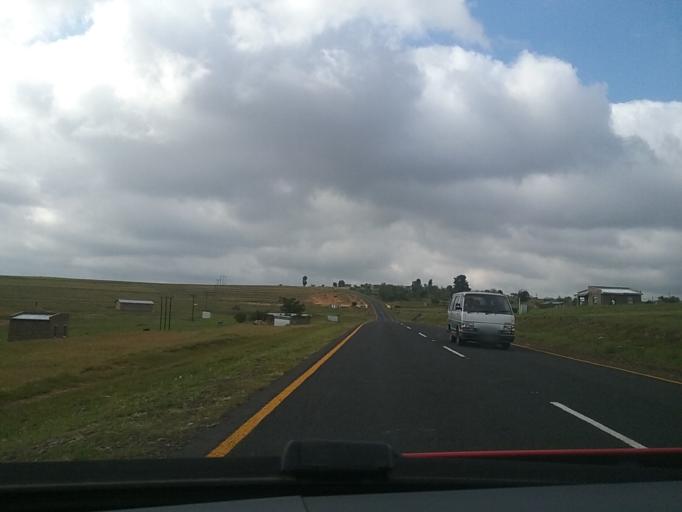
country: LS
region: Berea
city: Teyateyaneng
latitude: -29.1902
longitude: 27.8048
